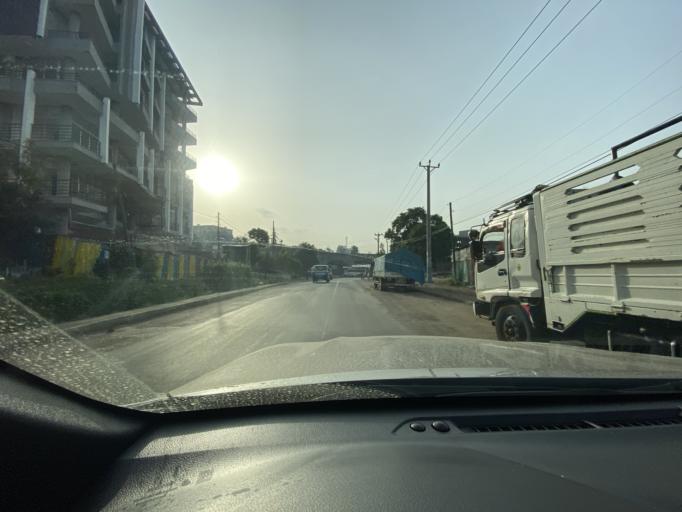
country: ET
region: Adis Abeba
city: Addis Ababa
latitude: 9.0215
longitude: 38.7215
